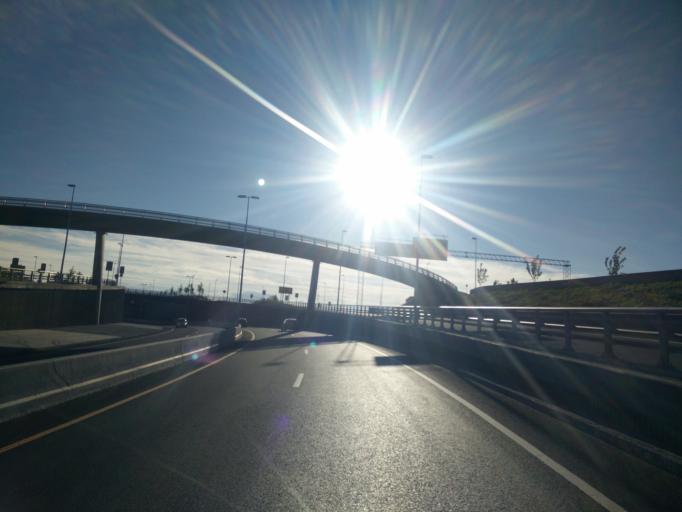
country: NO
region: Sor-Trondelag
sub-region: Trondheim
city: Trondheim
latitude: 63.4316
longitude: 10.4906
